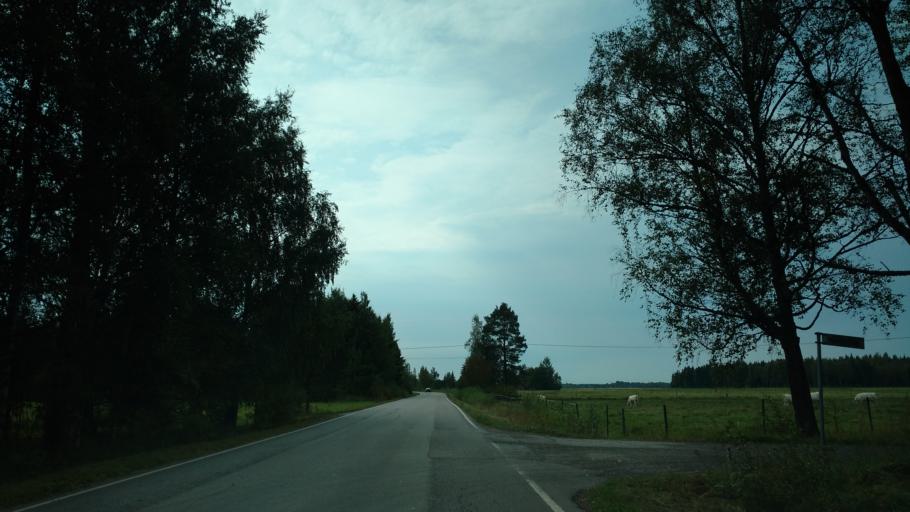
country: FI
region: Varsinais-Suomi
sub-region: Loimaa
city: Koski Tl
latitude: 60.6830
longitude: 23.1603
